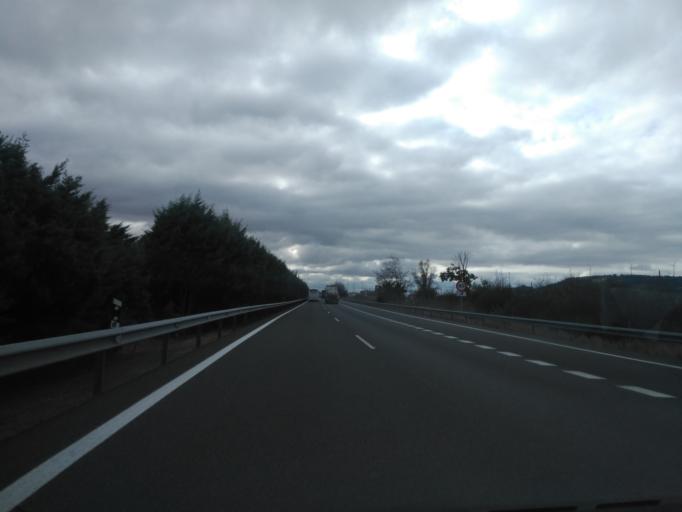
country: ES
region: Castille and Leon
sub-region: Provincia de Palencia
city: Venta de Banos
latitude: 41.9160
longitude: -4.5100
